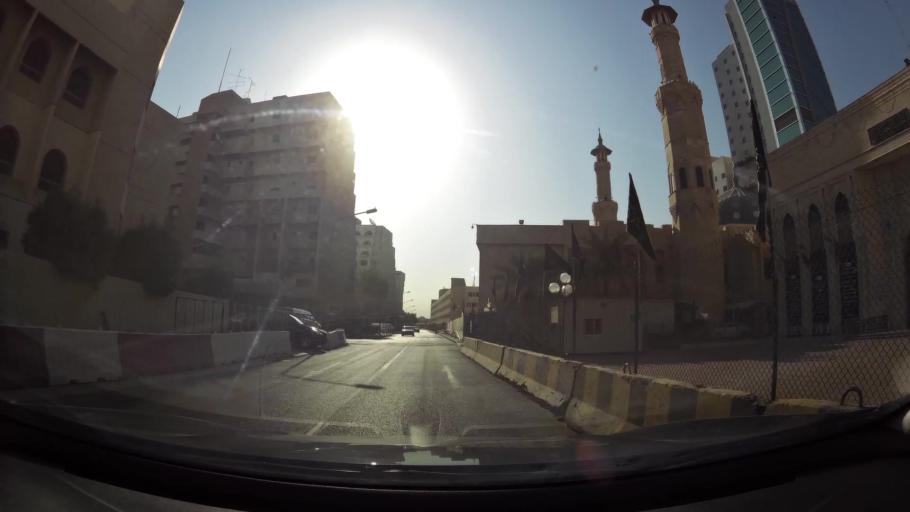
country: KW
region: Al Asimah
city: Kuwait City
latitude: 29.3753
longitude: 47.9798
